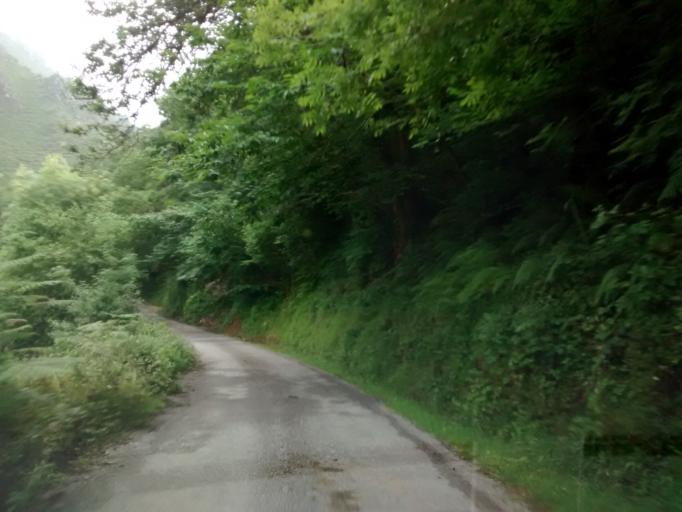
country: ES
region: Asturias
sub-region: Province of Asturias
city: Pilona
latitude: 43.2716
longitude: -5.3447
